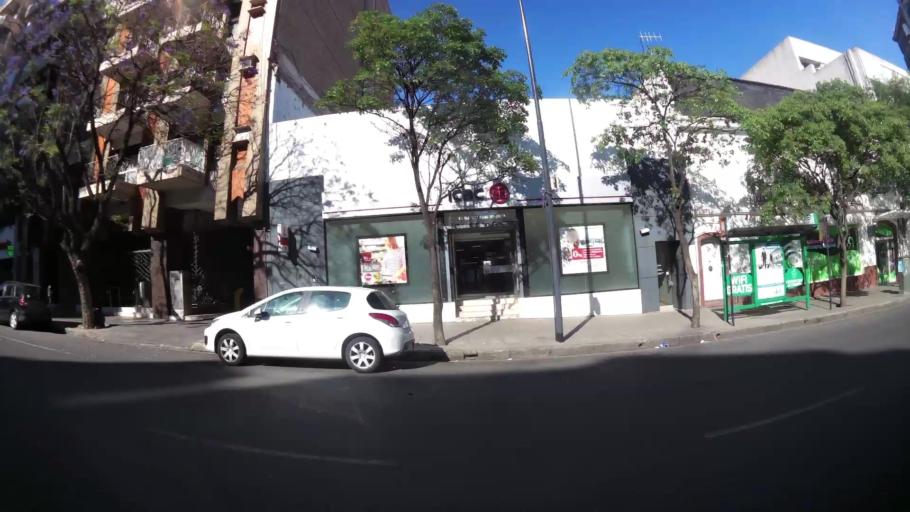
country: AR
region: Cordoba
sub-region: Departamento de Capital
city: Cordoba
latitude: -31.4250
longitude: -64.1866
